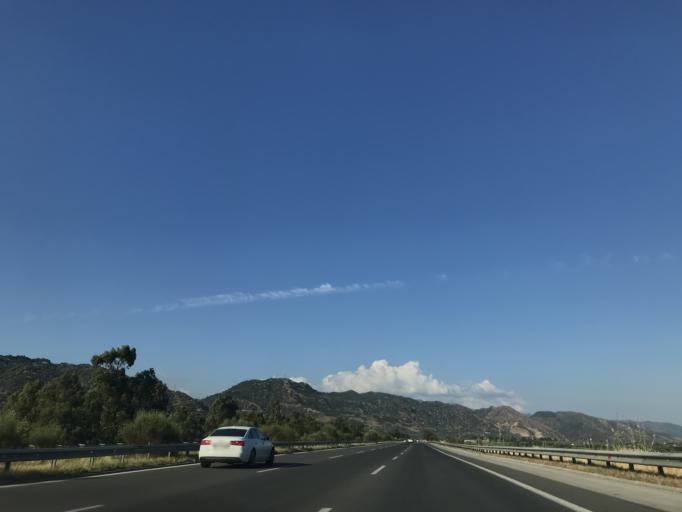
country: TR
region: Aydin
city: Incirliova
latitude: 37.8711
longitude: 27.6661
